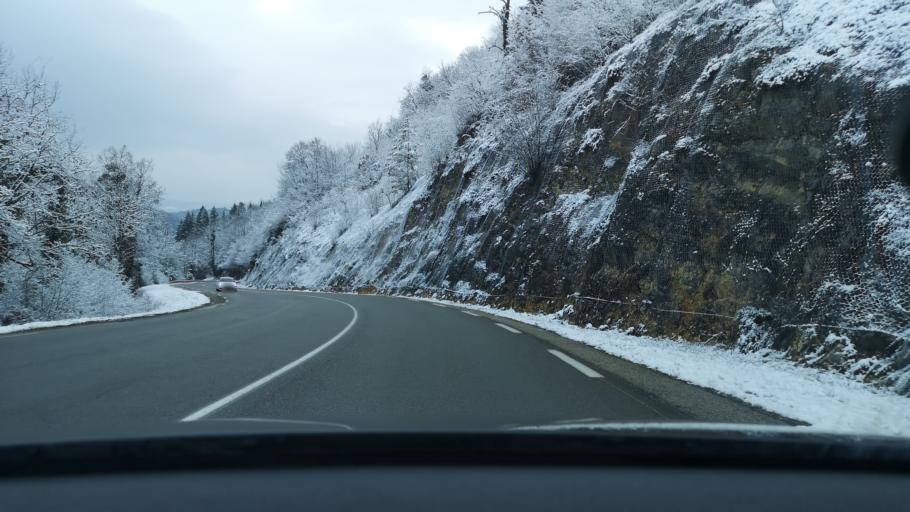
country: FR
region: Franche-Comte
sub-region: Departement du Jura
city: Moirans-en-Montagne
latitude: 46.3718
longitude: 5.7054
